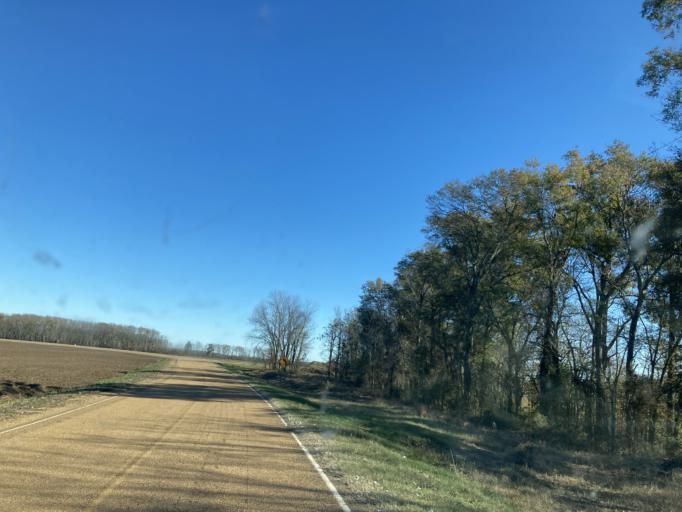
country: US
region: Mississippi
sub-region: Yazoo County
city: Yazoo City
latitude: 32.7399
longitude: -90.6382
